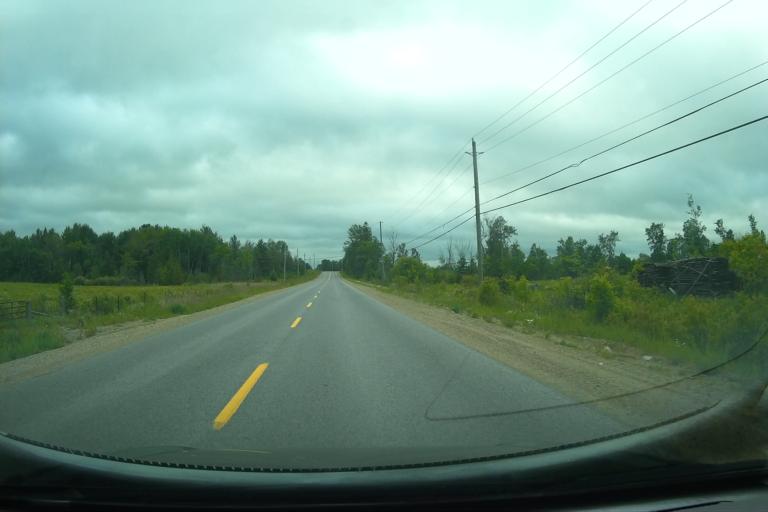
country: CA
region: Ontario
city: Pembroke
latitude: 45.4972
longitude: -77.1536
